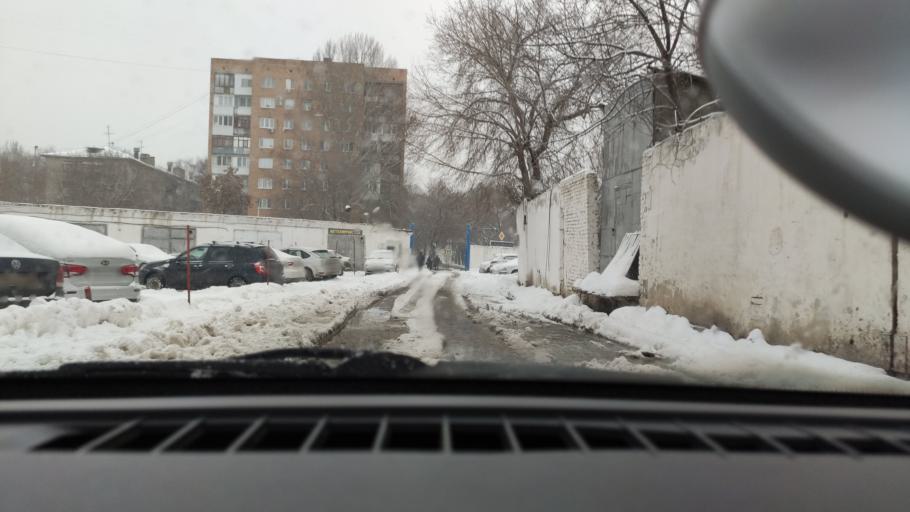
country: RU
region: Samara
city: Smyshlyayevka
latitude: 53.2198
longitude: 50.2753
